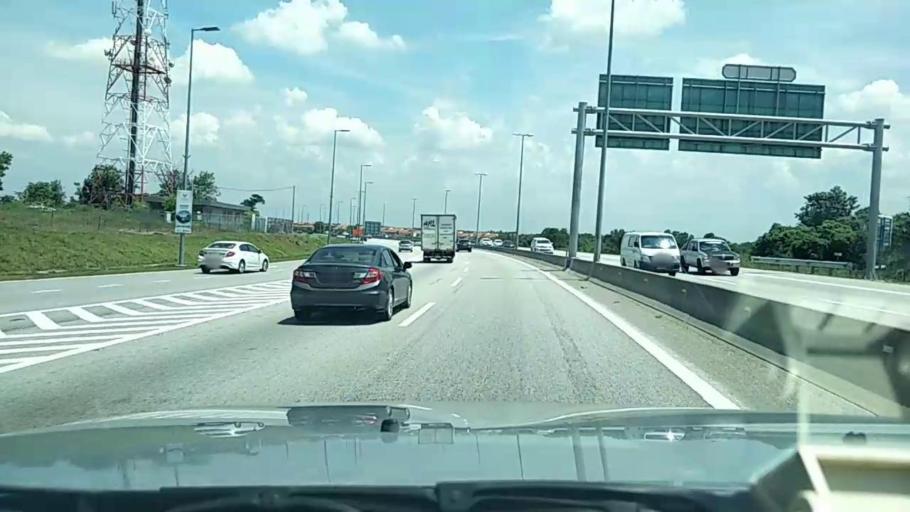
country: MY
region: Putrajaya
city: Putrajaya
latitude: 2.9399
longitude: 101.6274
